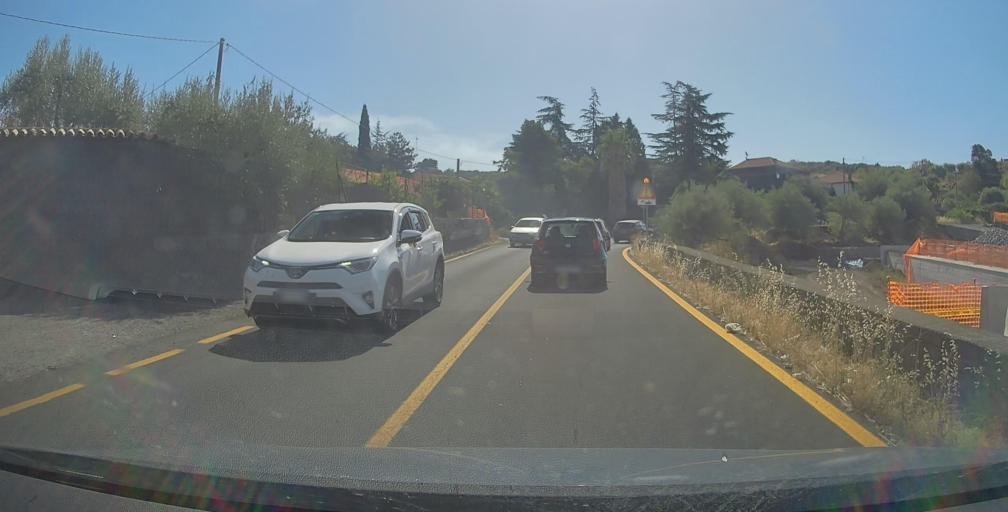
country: IT
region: Sicily
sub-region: Catania
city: Adrano
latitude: 37.6956
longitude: 14.8418
